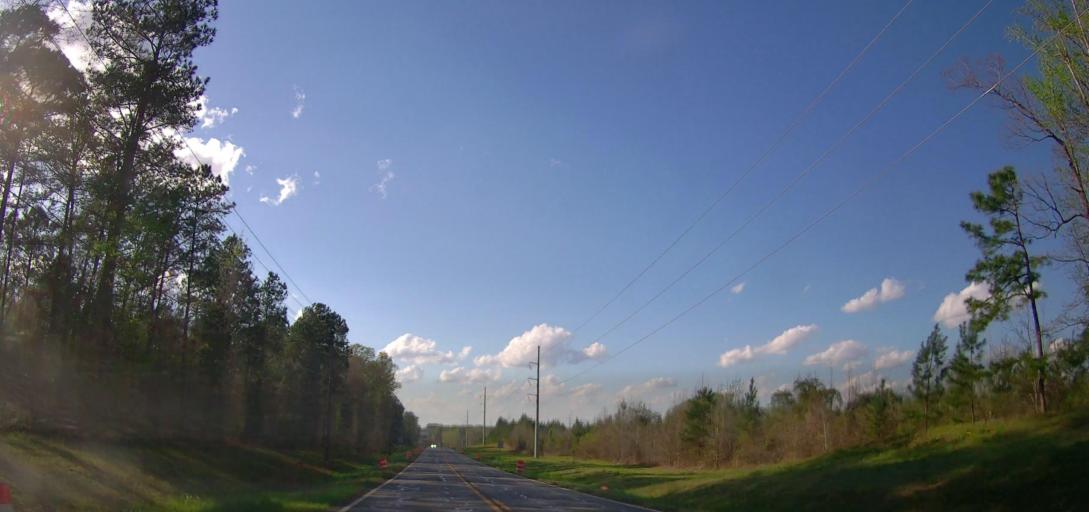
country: US
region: Georgia
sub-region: Baldwin County
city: Milledgeville
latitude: 33.1419
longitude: -83.3330
